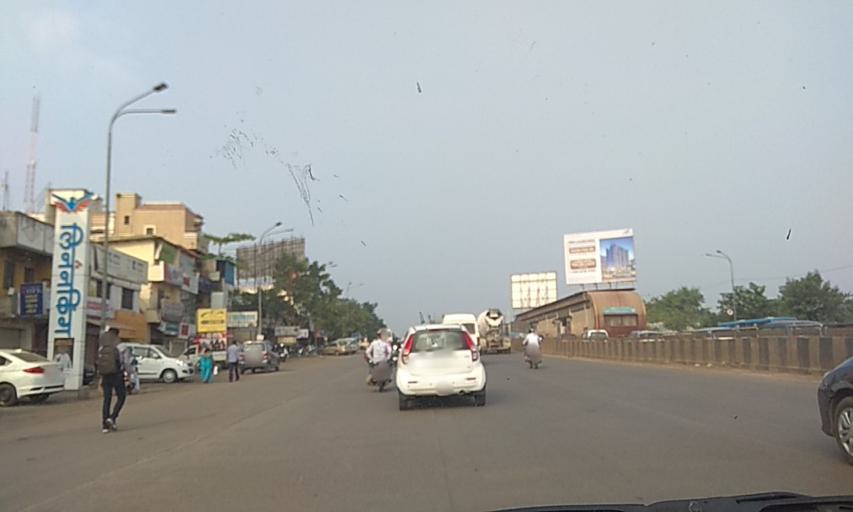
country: IN
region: Maharashtra
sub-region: Pune Division
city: Lohogaon
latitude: 18.5632
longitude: 73.9336
